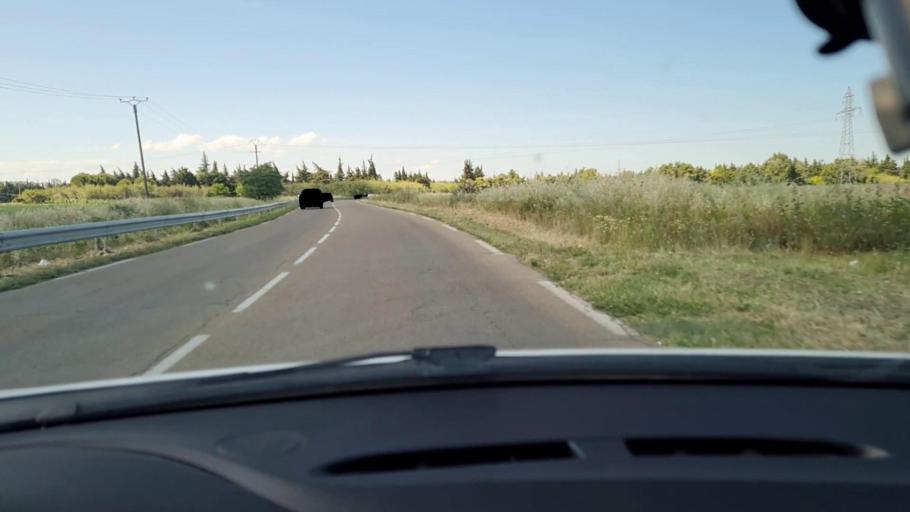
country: FR
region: Languedoc-Roussillon
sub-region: Departement du Gard
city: Caissargues
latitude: 43.7994
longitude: 4.3535
